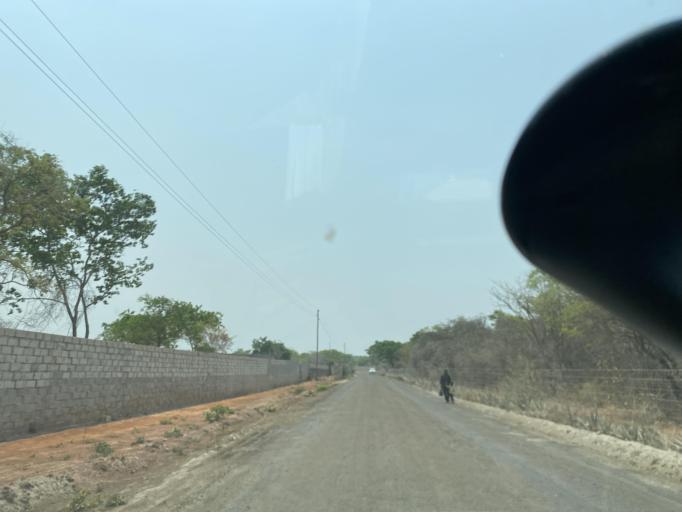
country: ZM
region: Lusaka
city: Lusaka
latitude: -15.5126
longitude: 28.4440
